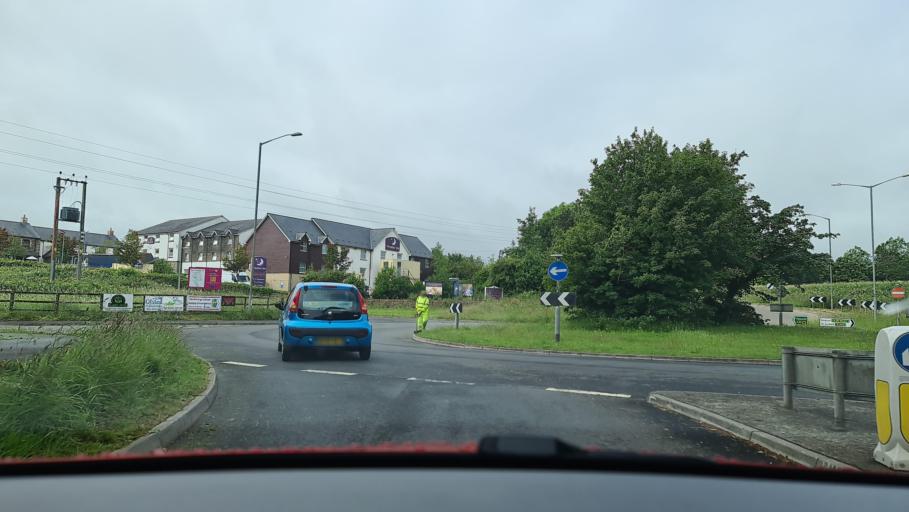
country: GB
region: England
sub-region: Cornwall
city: Liskeard
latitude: 50.4496
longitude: -4.4498
